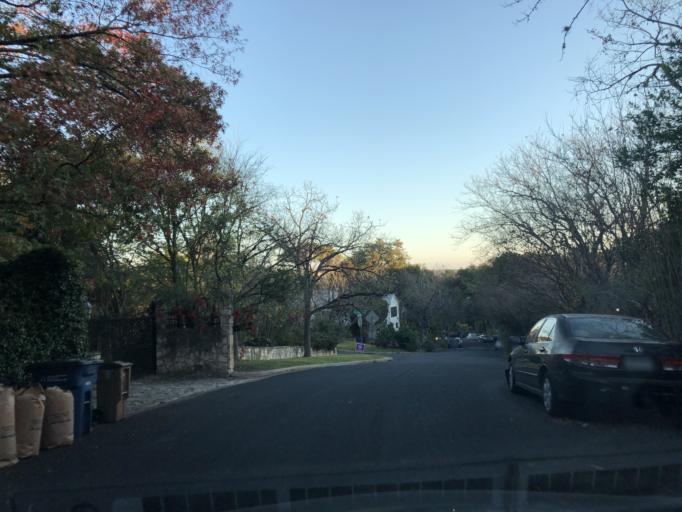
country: US
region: Texas
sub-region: Travis County
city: Austin
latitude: 30.2479
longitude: -97.7410
